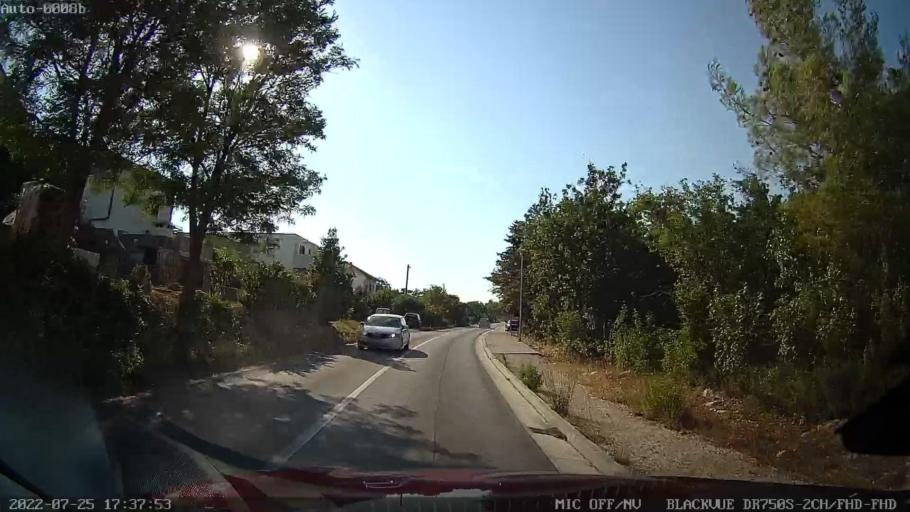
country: HR
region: Zadarska
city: Posedarje
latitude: 44.2072
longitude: 15.4675
